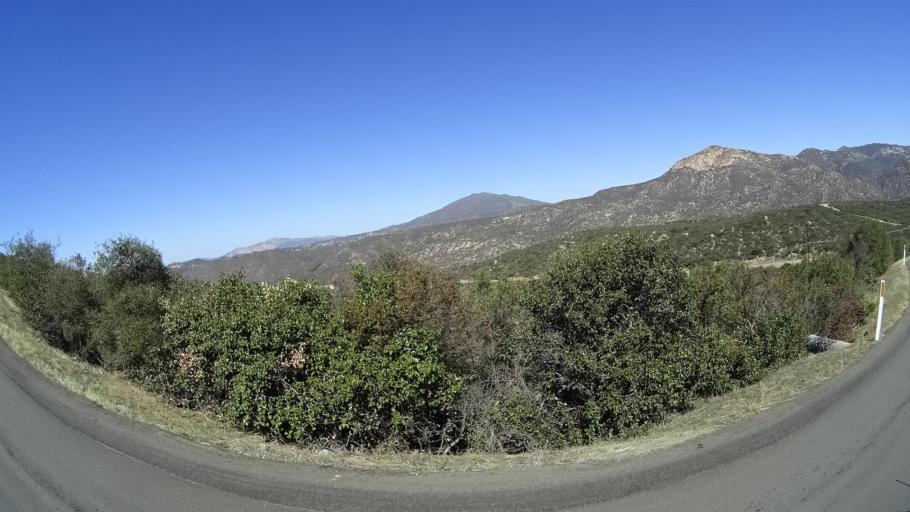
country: US
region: California
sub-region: San Diego County
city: Alpine
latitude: 32.7775
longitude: -116.7189
